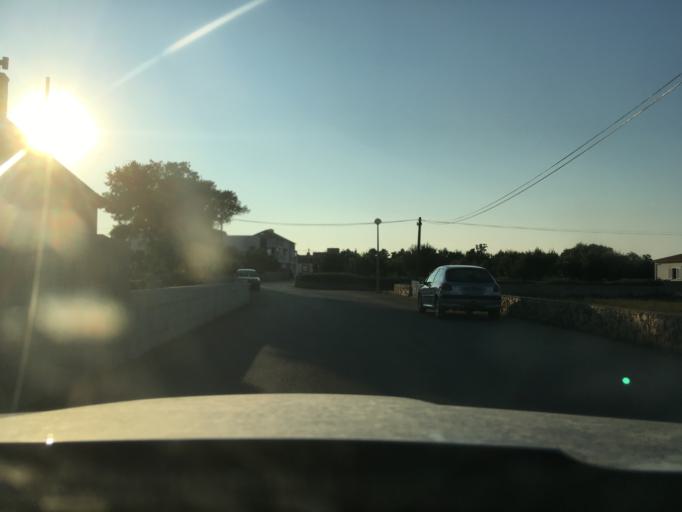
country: HR
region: Zadarska
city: Vir
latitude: 44.3043
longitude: 15.0799
